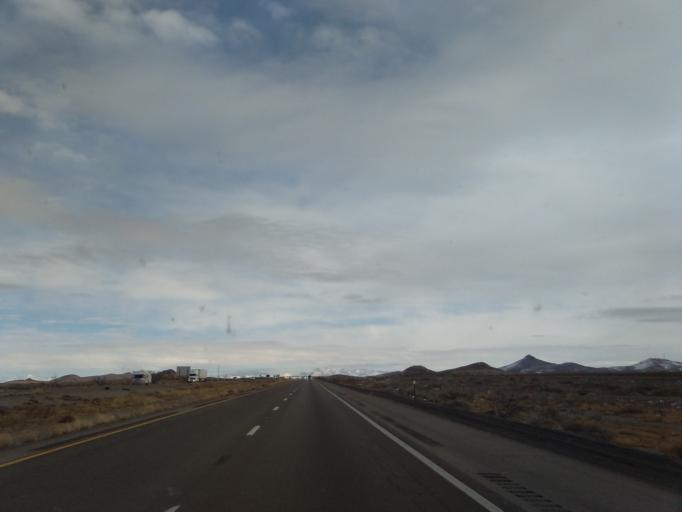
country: US
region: New Mexico
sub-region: Hidalgo County
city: Lordsburg
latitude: 32.3104
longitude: -108.8276
